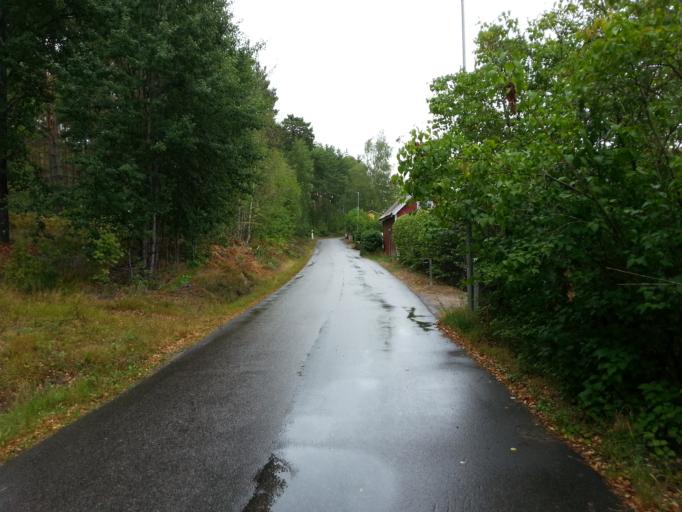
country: SE
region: OEstergoetland
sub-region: Norrkopings Kommun
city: Krokek
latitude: 58.6719
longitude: 16.3617
